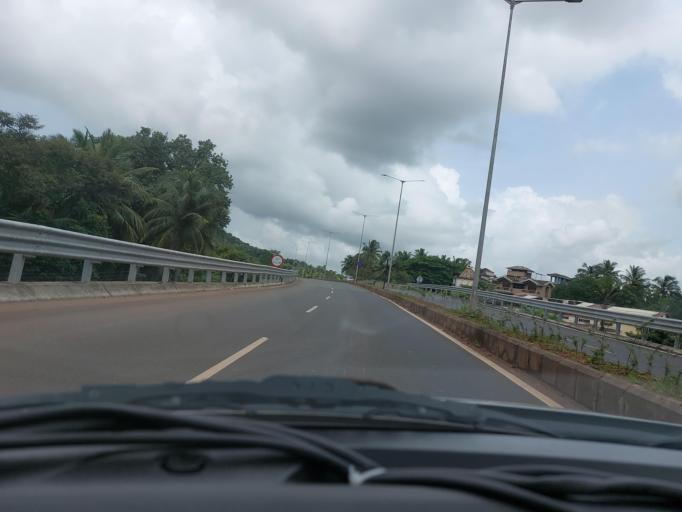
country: IN
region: Goa
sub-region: North Goa
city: Queula
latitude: 15.3844
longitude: 74.0016
